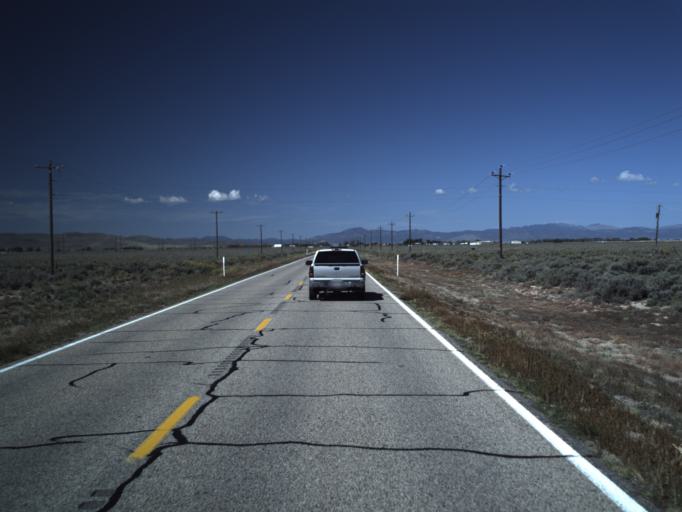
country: US
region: Utah
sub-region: Washington County
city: Enterprise
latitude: 37.6977
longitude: -113.6235
